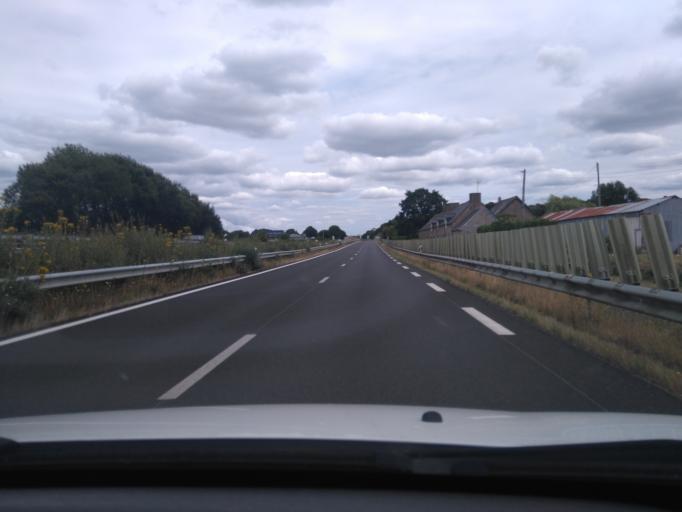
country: FR
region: Brittany
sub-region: Departement des Cotes-d'Armor
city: Pedernec
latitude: 48.5837
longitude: -3.2444
